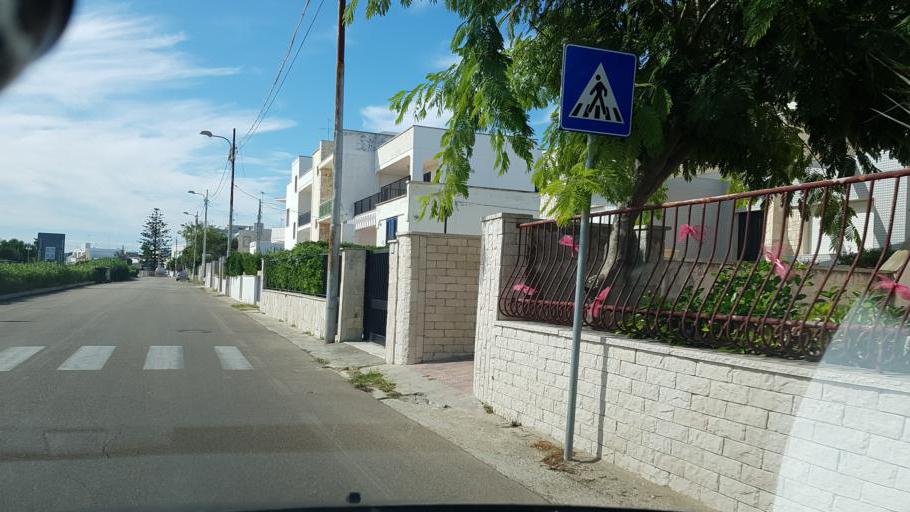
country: IT
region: Apulia
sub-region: Provincia di Lecce
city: Borgagne
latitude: 40.2782
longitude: 18.4303
